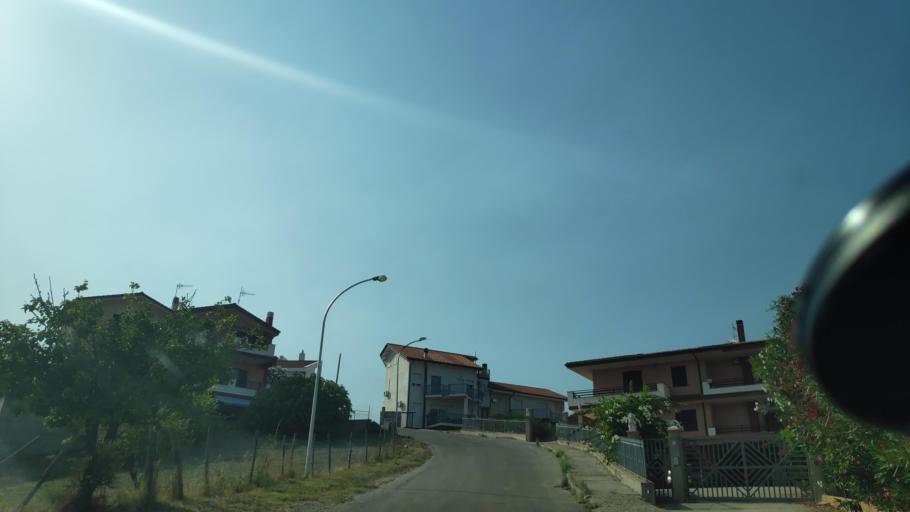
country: IT
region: Calabria
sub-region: Provincia di Catanzaro
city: Santa Caterina dello Ionio Marina
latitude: 38.5325
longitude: 16.5669
